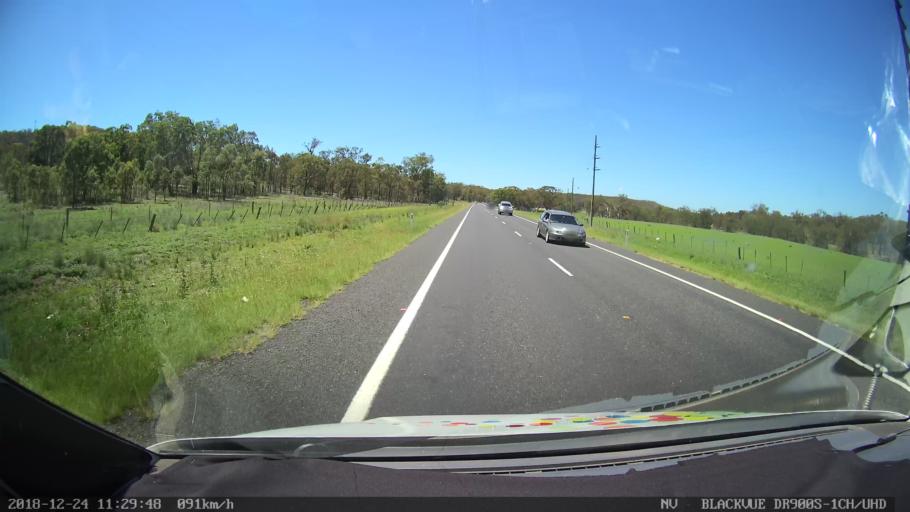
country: AU
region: New South Wales
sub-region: Upper Hunter Shire
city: Merriwa
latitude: -32.1967
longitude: 150.4651
